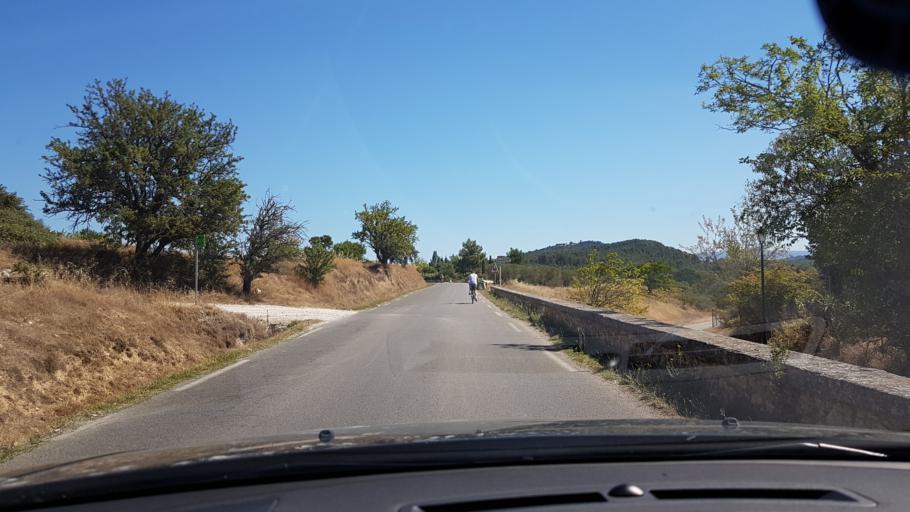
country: FR
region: Provence-Alpes-Cote d'Azur
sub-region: Departement des Bouches-du-Rhone
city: Eygalieres
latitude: 43.7640
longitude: 4.9545
